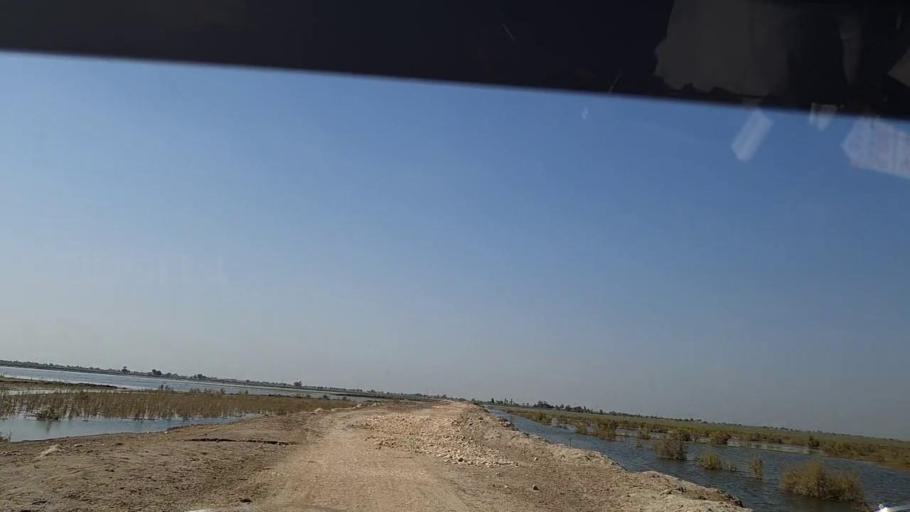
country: PK
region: Sindh
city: Tangwani
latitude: 28.3544
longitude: 69.0390
